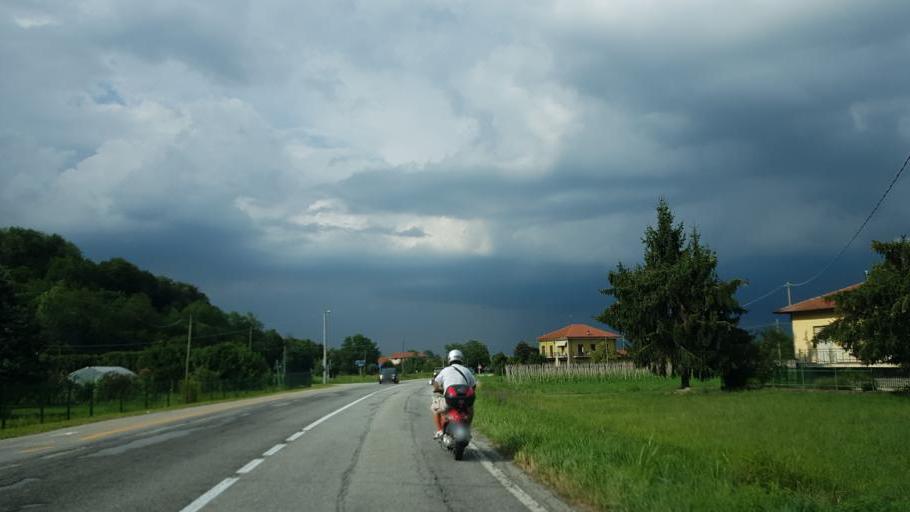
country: IT
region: Piedmont
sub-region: Provincia di Cuneo
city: Vignolo
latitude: 44.3711
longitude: 7.4745
